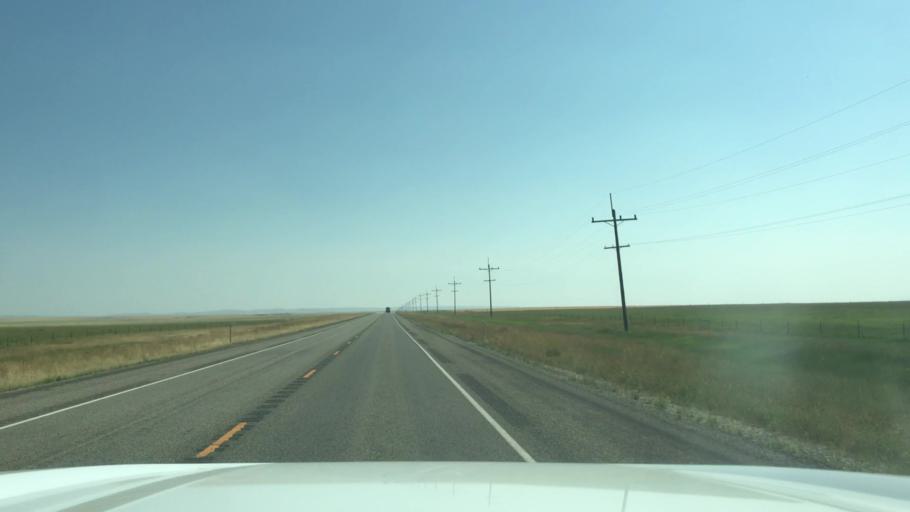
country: US
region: Montana
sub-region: Wheatland County
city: Harlowton
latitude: 46.5149
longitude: -109.7659
